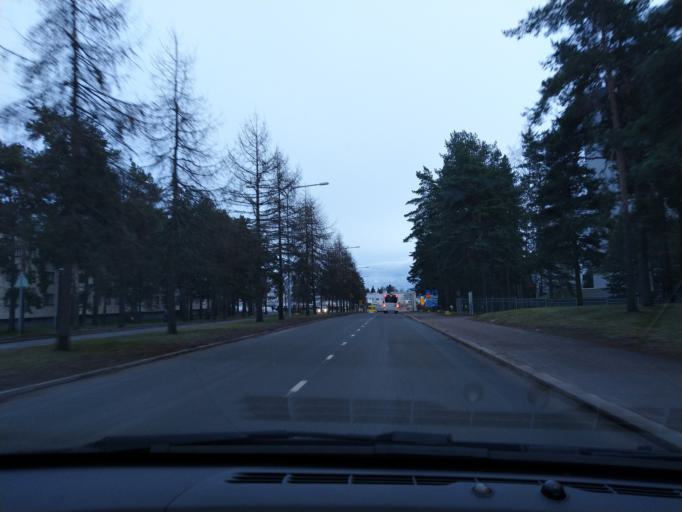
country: FI
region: Uusimaa
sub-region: Helsinki
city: Vantaa
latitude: 60.2378
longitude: 25.0786
